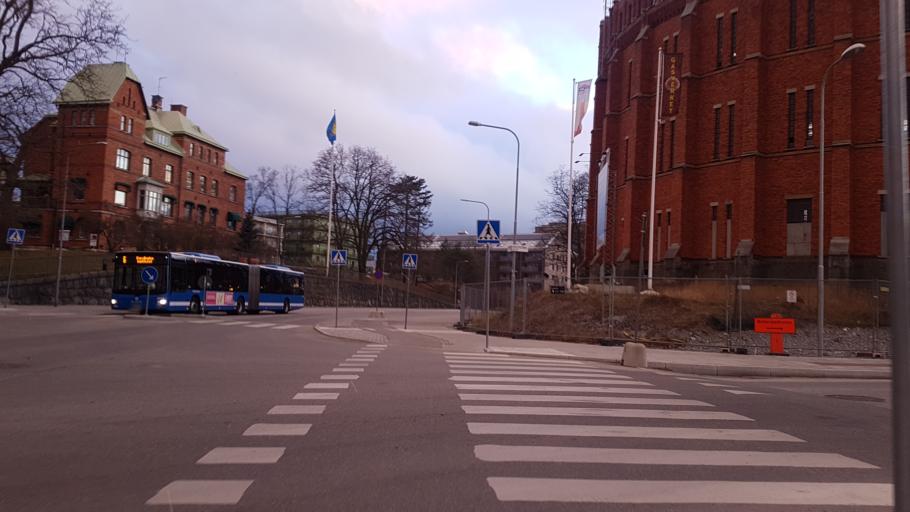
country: SE
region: Stockholm
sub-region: Stockholms Kommun
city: OEstermalm
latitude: 59.3569
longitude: 18.0888
